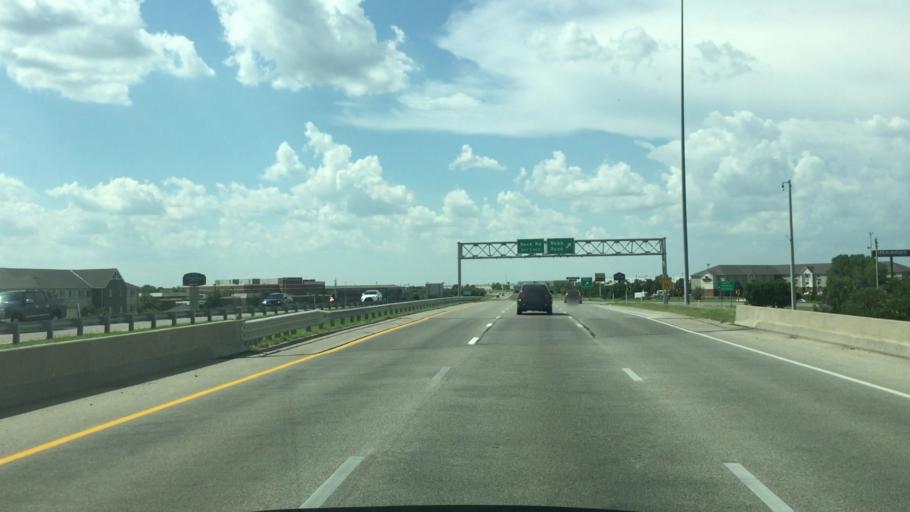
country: US
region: Kansas
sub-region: Sedgwick County
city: Bellaire
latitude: 37.7380
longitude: -97.2265
